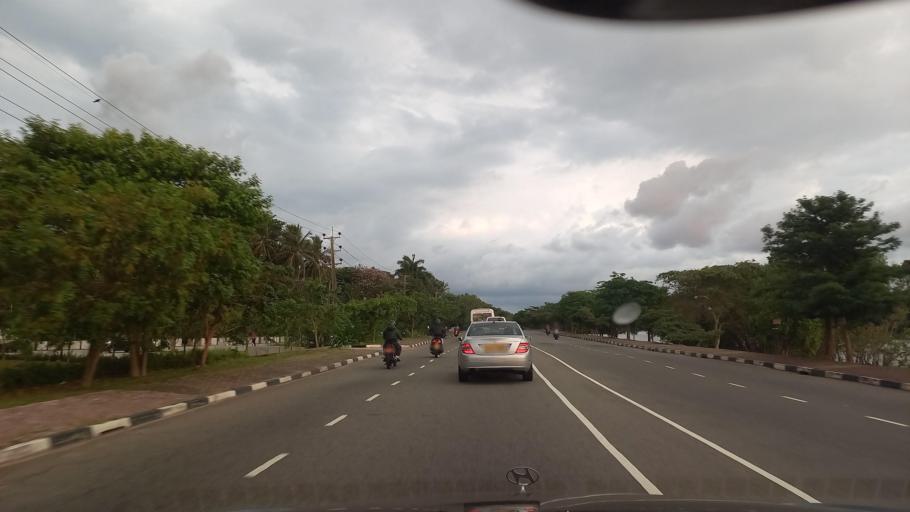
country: LK
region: Western
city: Battaramulla South
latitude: 6.8869
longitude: 79.9230
